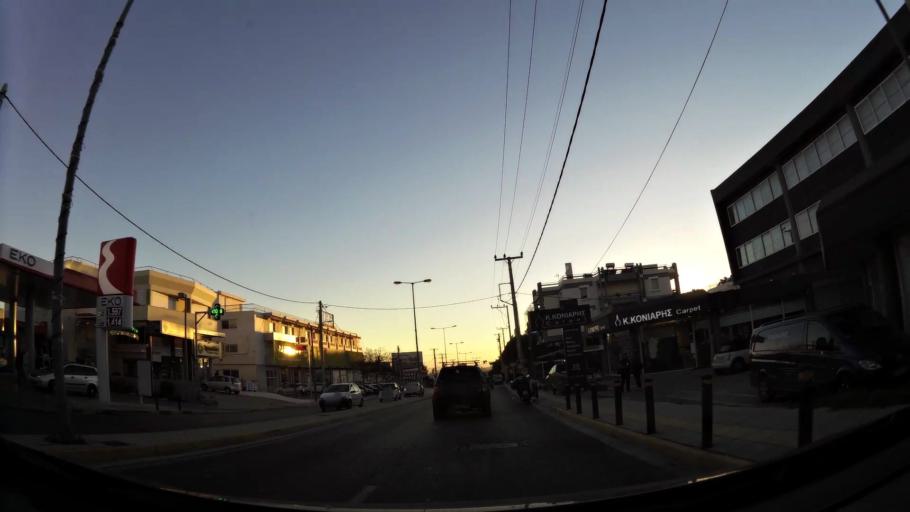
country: GR
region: Attica
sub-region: Nomarchia Athinas
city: Melissia
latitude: 38.0455
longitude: 23.8378
